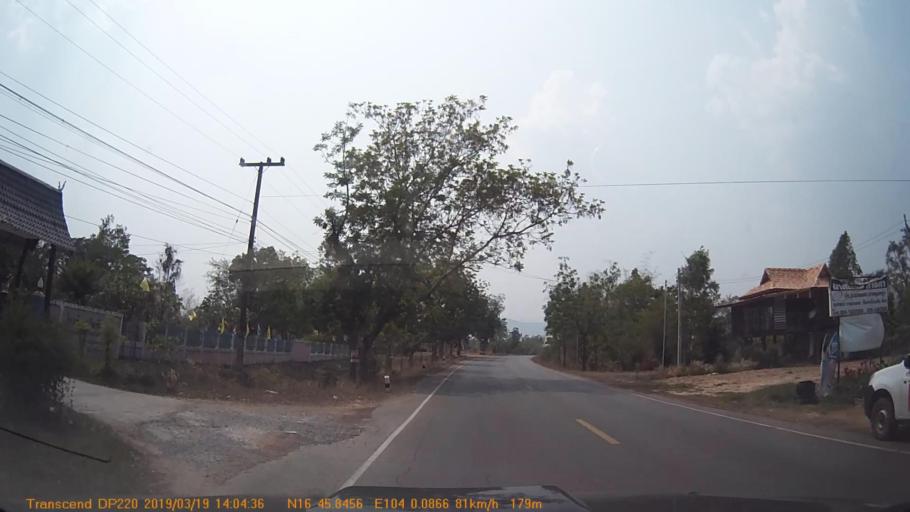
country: TH
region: Kalasin
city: Na Khu
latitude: 16.7642
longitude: 104.0010
